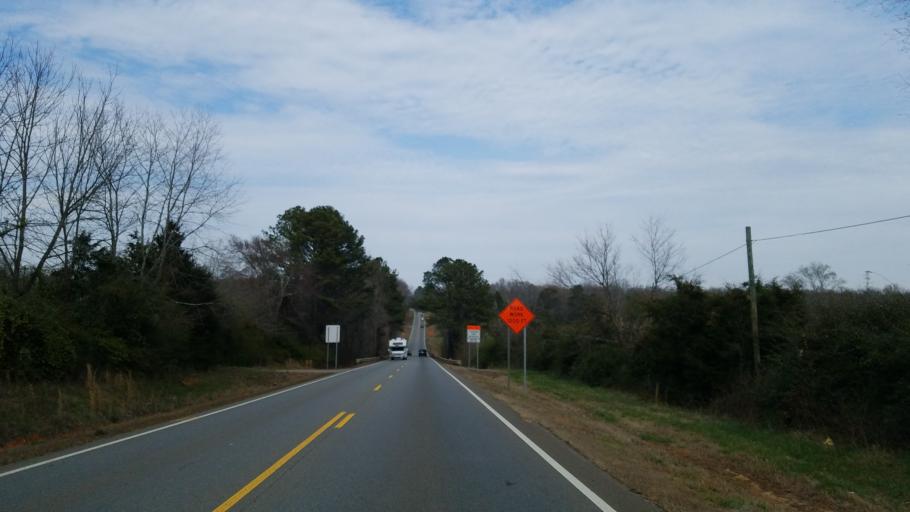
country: US
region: Georgia
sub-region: Cherokee County
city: Ball Ground
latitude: 34.2685
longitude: -84.3065
